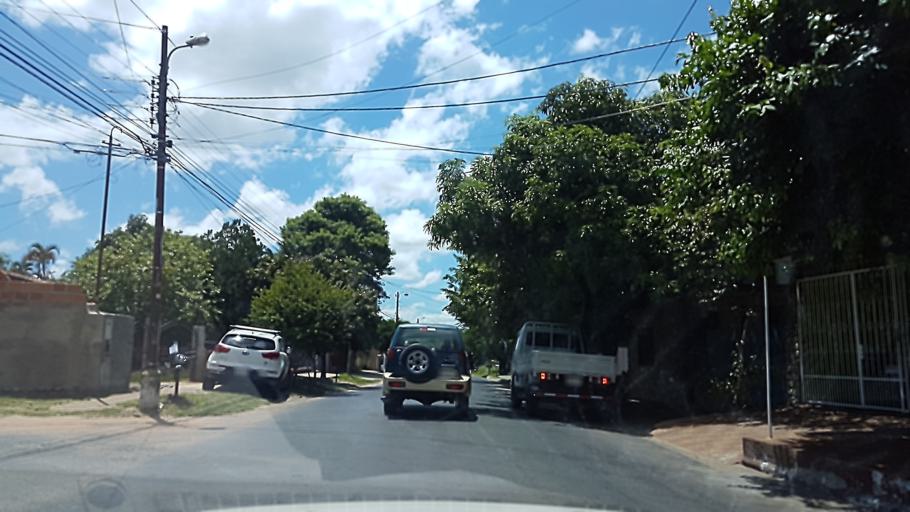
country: PY
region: Central
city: Colonia Mariano Roque Alonso
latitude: -25.2432
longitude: -57.5425
